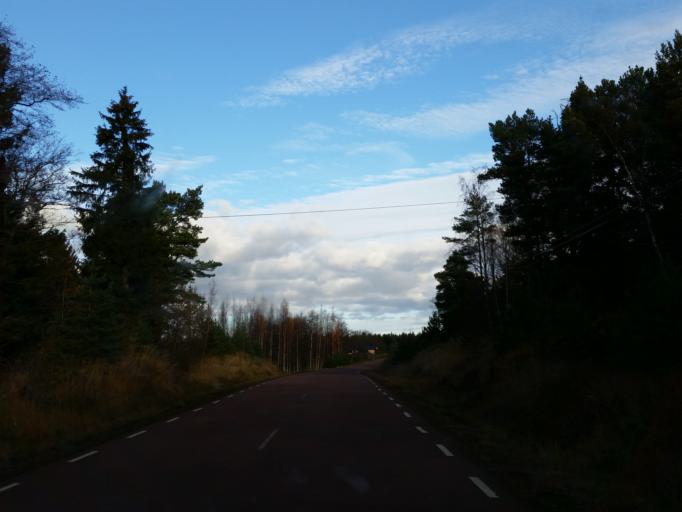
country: AX
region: Alands skaergard
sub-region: Foegloe
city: Foegloe
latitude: 60.0409
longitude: 20.5351
